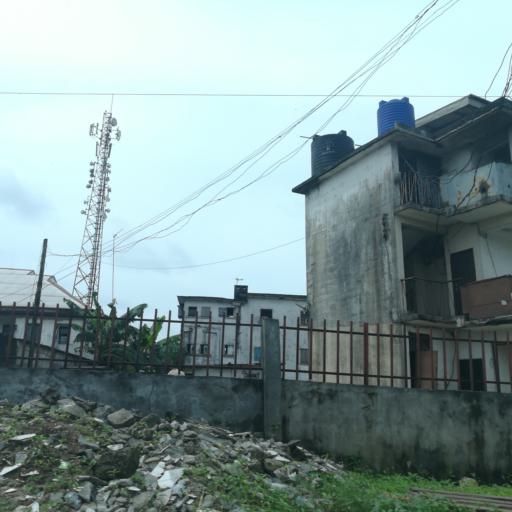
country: NG
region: Rivers
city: Port Harcourt
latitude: 4.8055
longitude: 7.0067
